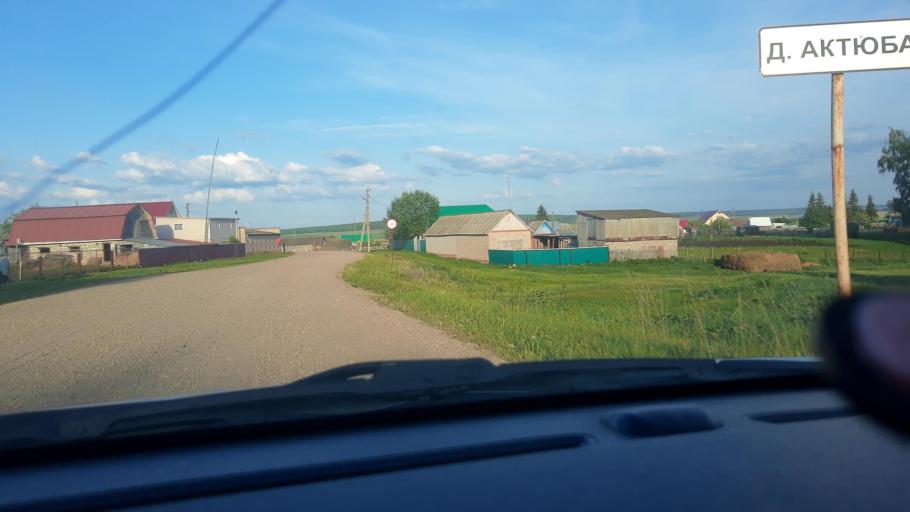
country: RU
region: Bashkortostan
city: Karmaskaly
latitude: 54.3802
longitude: 55.9362
